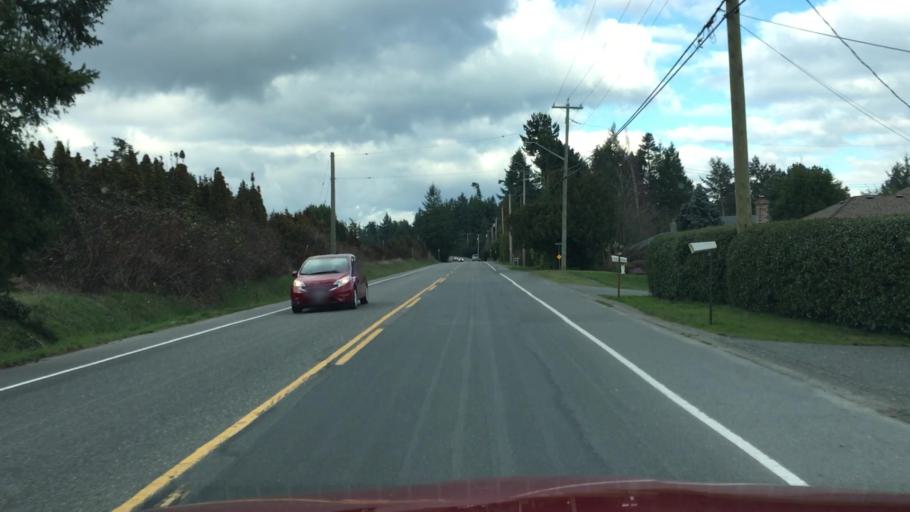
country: CA
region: British Columbia
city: North Saanich
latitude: 48.6021
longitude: -123.3961
